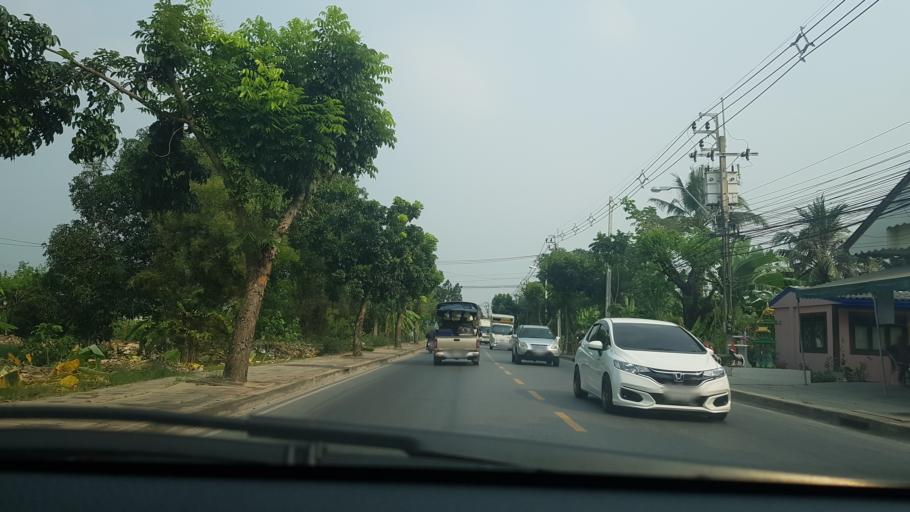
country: TH
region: Bangkok
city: Thawi Watthana
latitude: 13.7568
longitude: 100.3879
